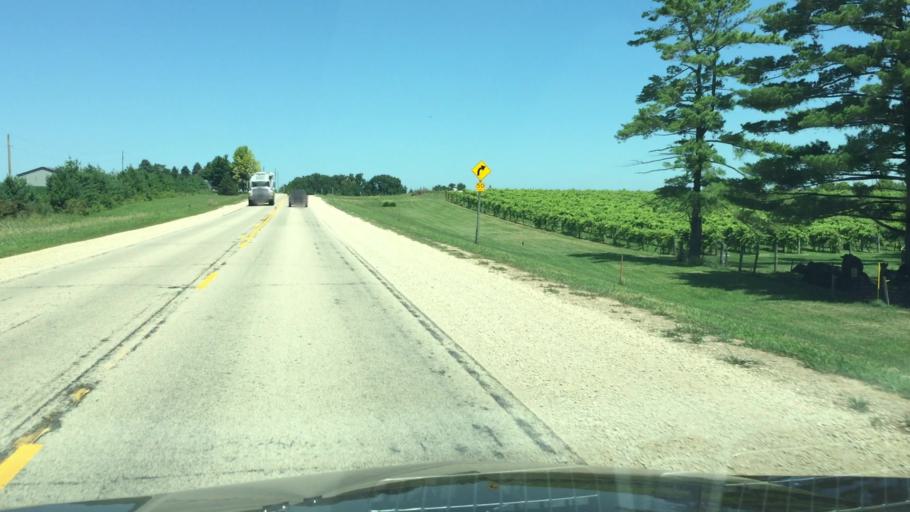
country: US
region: Iowa
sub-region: Cedar County
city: Mechanicsville
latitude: 41.9564
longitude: -91.1519
